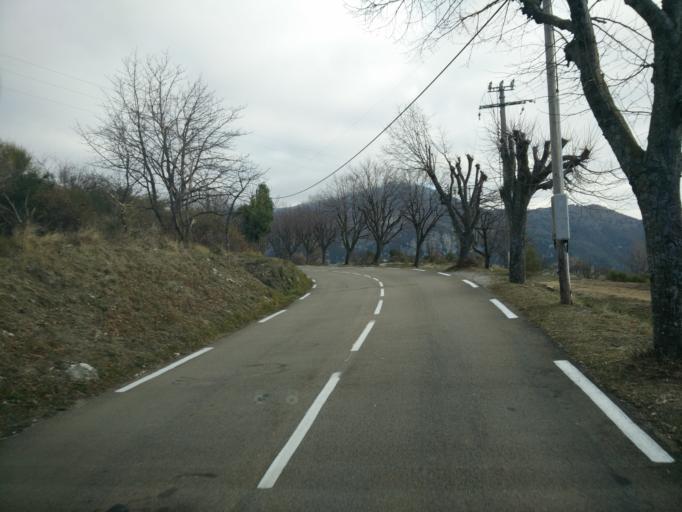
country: FR
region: Provence-Alpes-Cote d'Azur
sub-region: Departement des Alpes-Maritimes
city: Opio
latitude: 43.7224
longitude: 6.9787
